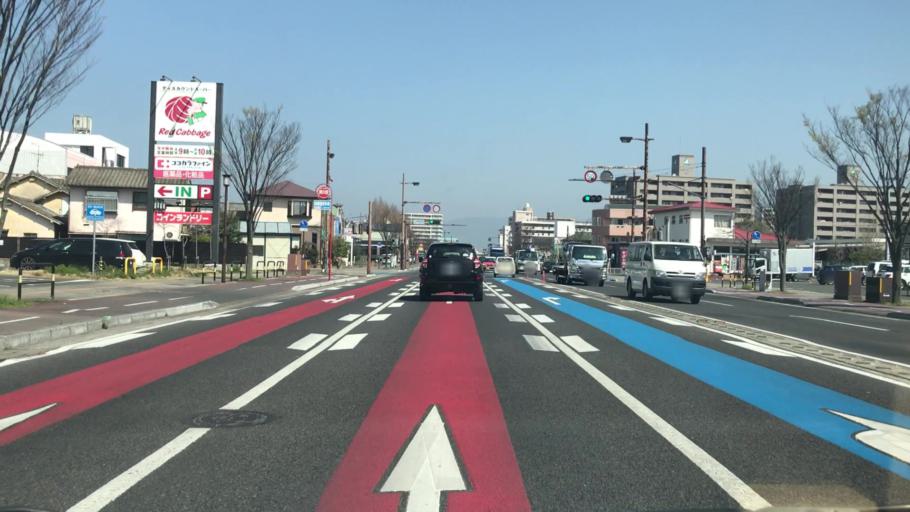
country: JP
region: Saga Prefecture
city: Saga-shi
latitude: 33.2568
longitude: 130.2929
